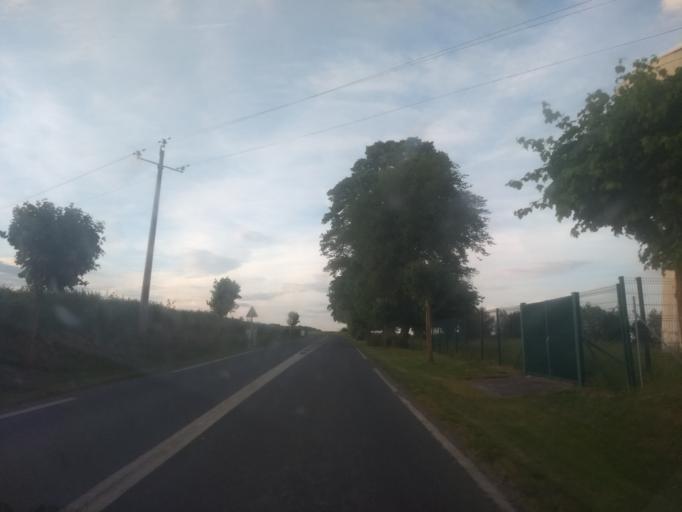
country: FR
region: Nord-Pas-de-Calais
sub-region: Departement du Pas-de-Calais
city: Bucquoy
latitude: 50.1220
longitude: 2.6935
